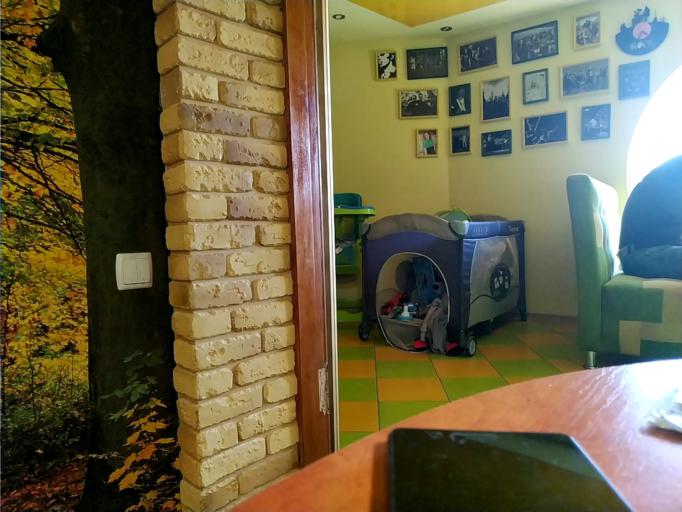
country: RU
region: Rjazan
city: Putyatino
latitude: 53.9901
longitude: 41.2652
